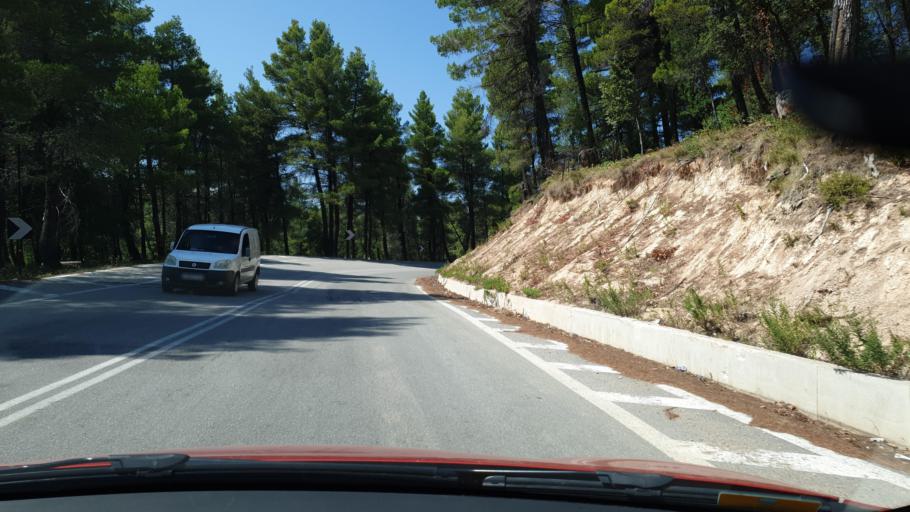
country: GR
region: Central Greece
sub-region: Nomos Evvoias
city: Politika
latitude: 38.6516
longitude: 23.5632
